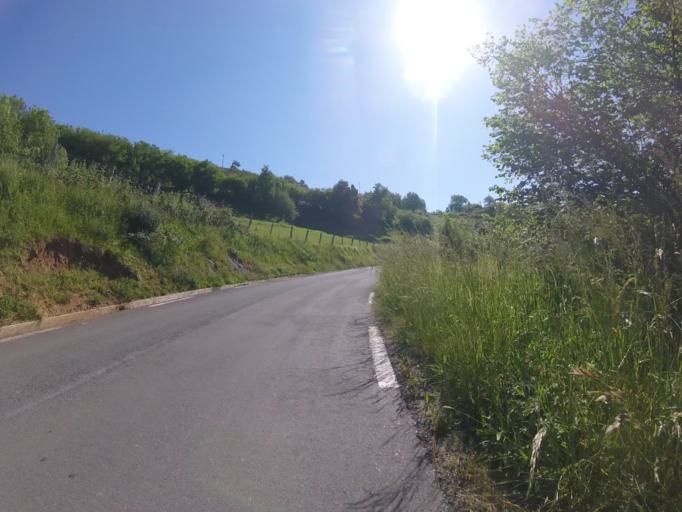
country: ES
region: Basque Country
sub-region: Provincia de Guipuzcoa
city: Beizama
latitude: 43.1243
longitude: -2.1879
